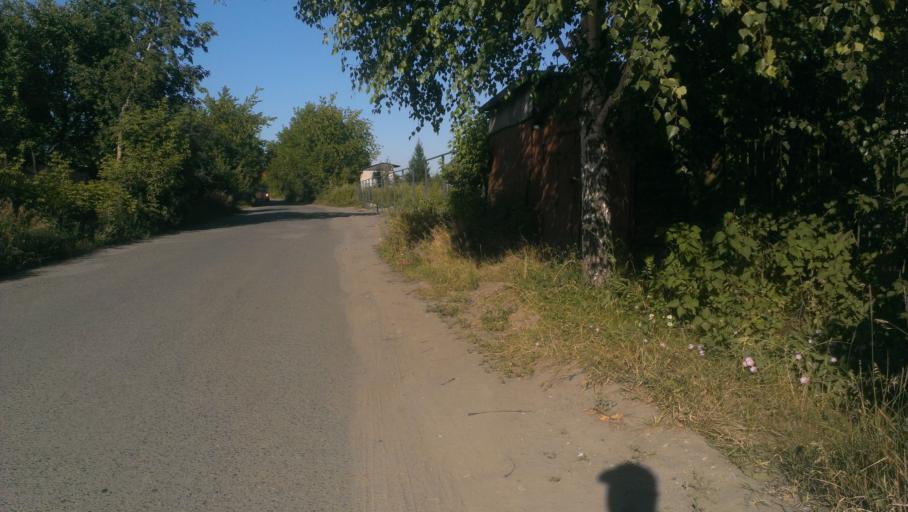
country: RU
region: Altai Krai
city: Novosilikatnyy
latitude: 53.3228
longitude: 83.6828
